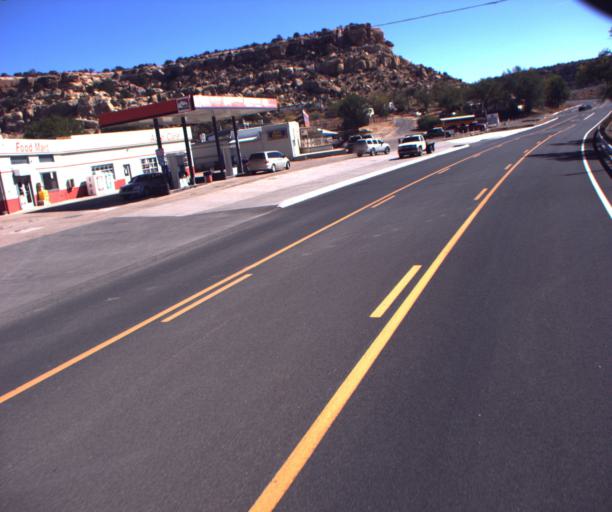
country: US
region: Arizona
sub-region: Navajo County
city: First Mesa
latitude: 35.8154
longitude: -110.2060
